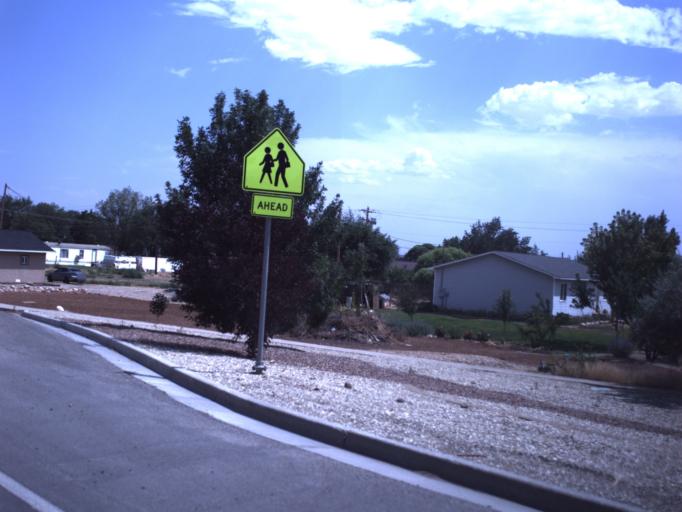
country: US
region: Utah
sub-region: Duchesne County
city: Roosevelt
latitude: 40.3022
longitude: -109.9988
